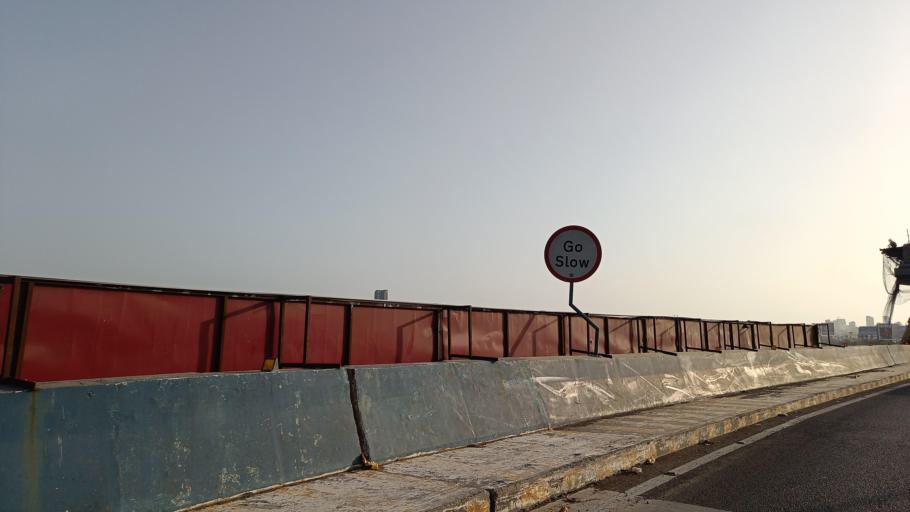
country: IN
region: Maharashtra
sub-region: Mumbai Suburban
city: Mumbai
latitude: 19.0528
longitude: 72.8475
